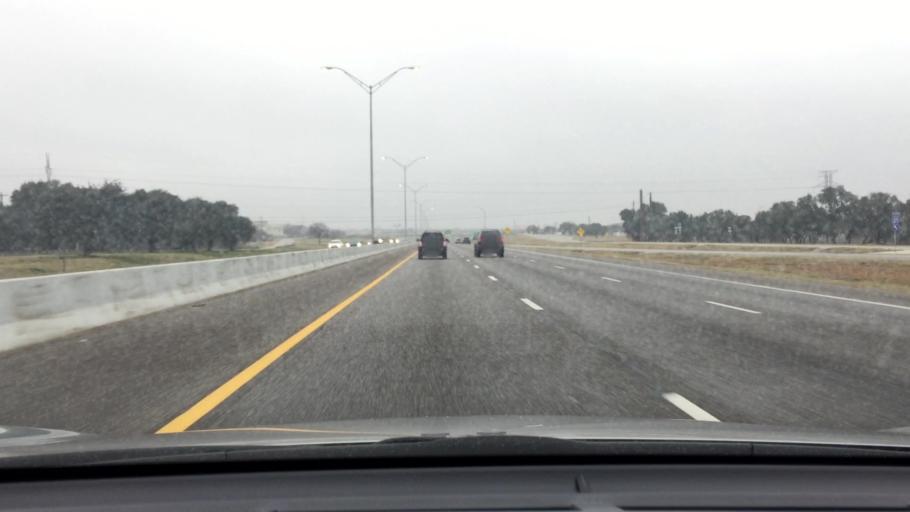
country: US
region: Texas
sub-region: Williamson County
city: Georgetown
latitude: 30.6153
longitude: -97.6880
